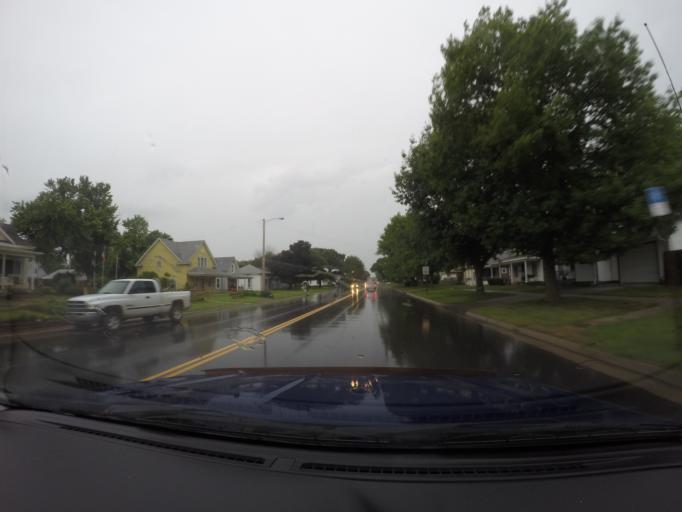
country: US
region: Kansas
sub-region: Cloud County
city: Concordia
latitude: 39.5716
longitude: -97.6511
